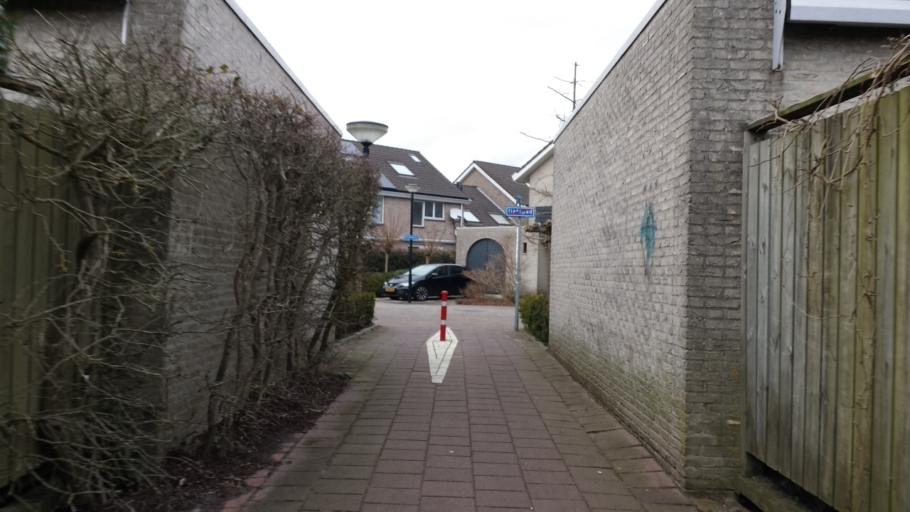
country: NL
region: South Holland
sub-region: Gemeente Gouda
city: Bloemendaal
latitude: 52.0278
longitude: 4.6968
